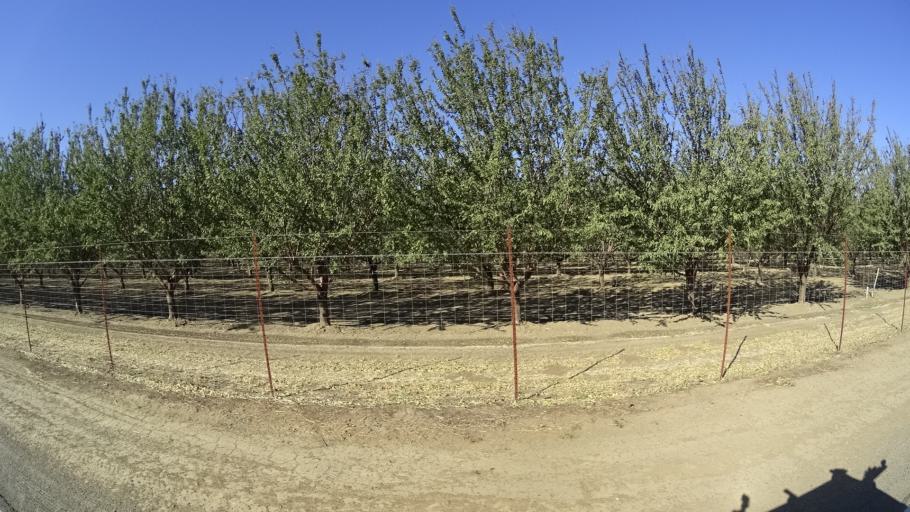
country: US
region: California
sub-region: Yolo County
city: Woodland
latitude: 38.7012
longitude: -121.8630
